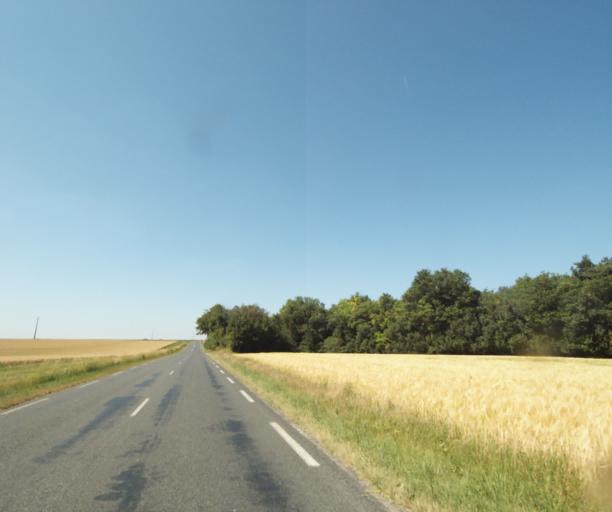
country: FR
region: Ile-de-France
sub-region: Departement de Seine-et-Marne
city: La Chapelle-la-Reine
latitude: 48.2930
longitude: 2.5765
